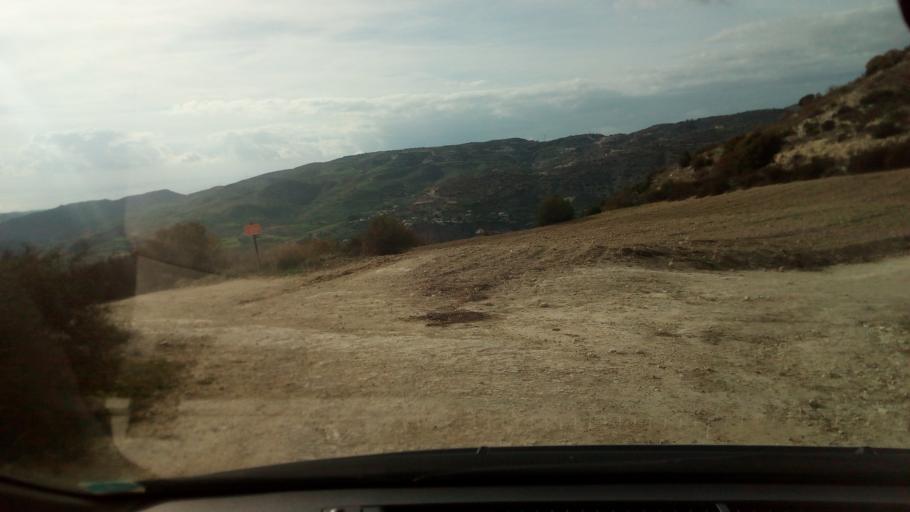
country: CY
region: Pafos
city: Mesogi
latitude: 34.7981
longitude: 32.5412
